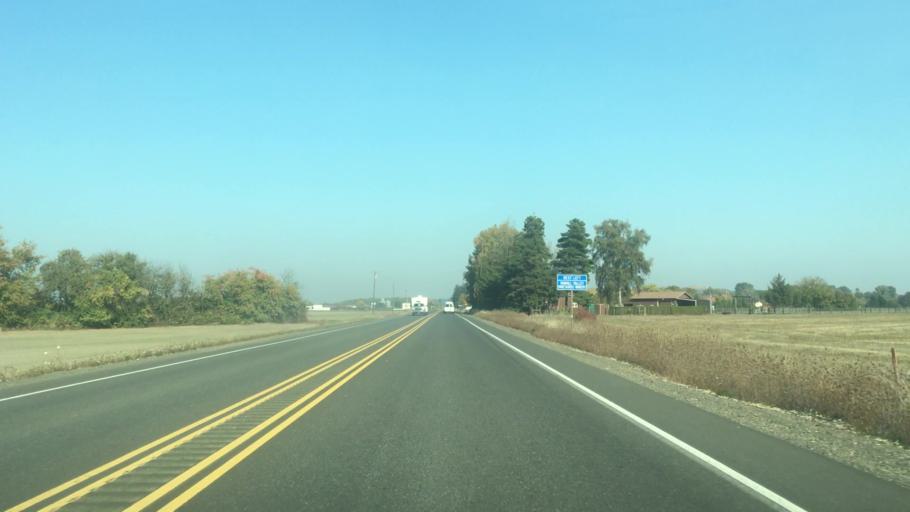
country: US
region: Oregon
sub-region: Yamhill County
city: Amity
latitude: 45.1502
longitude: -123.2729
